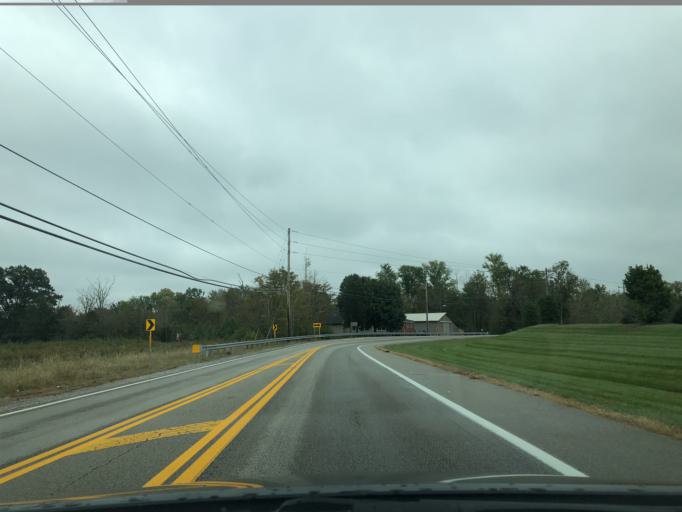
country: US
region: Ohio
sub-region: Hamilton County
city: Loveland
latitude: 39.2580
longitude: -84.2387
